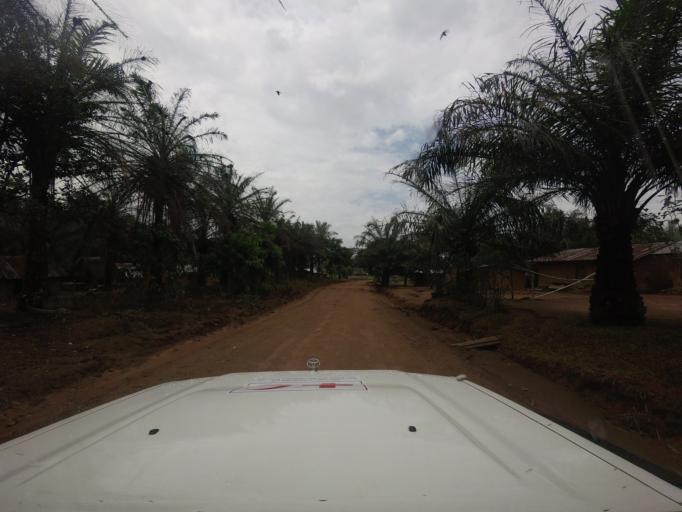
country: SL
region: Eastern Province
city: Buedu
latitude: 8.3294
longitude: -10.2077
